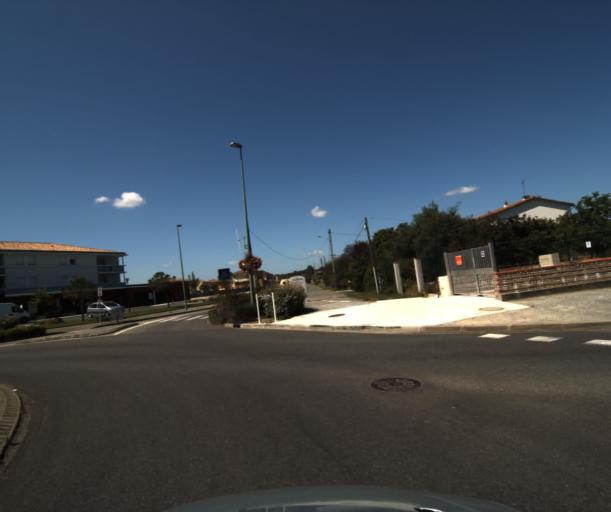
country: FR
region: Midi-Pyrenees
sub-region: Departement de la Haute-Garonne
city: Eaunes
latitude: 43.4283
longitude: 1.3544
